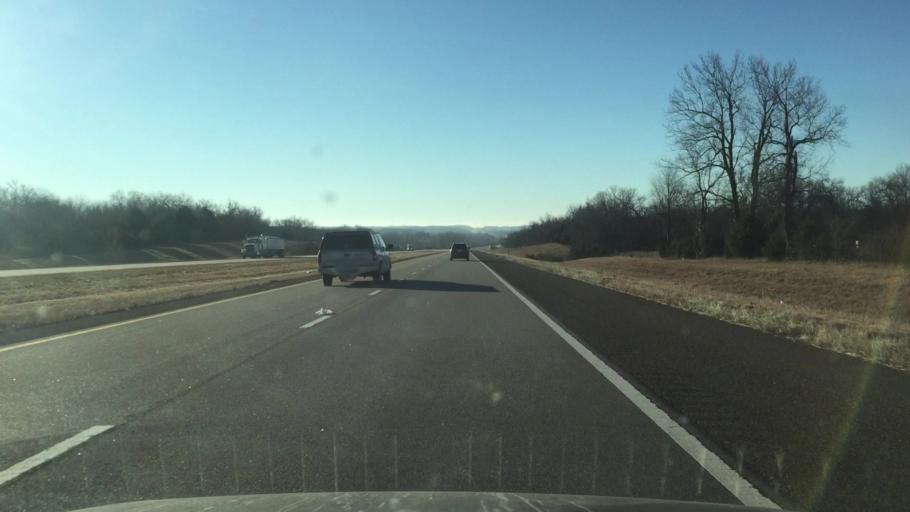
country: US
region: Kansas
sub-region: Johnson County
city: Spring Hill
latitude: 38.7152
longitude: -94.8347
